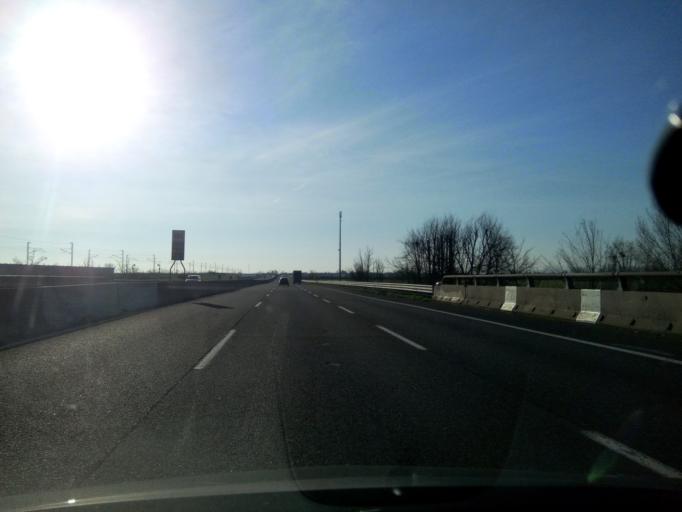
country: IT
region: Emilia-Romagna
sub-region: Provincia di Reggio Emilia
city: Roncocesi
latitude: 44.7490
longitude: 10.5597
